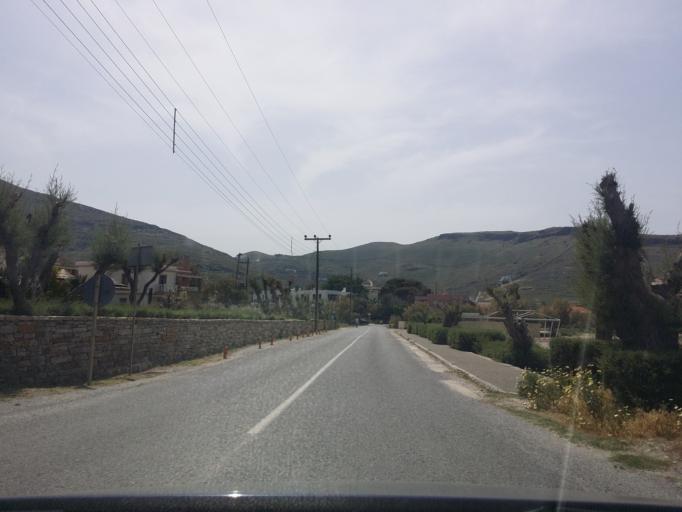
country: GR
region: South Aegean
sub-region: Nomos Kykladon
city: Kea
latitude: 37.6582
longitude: 24.3168
